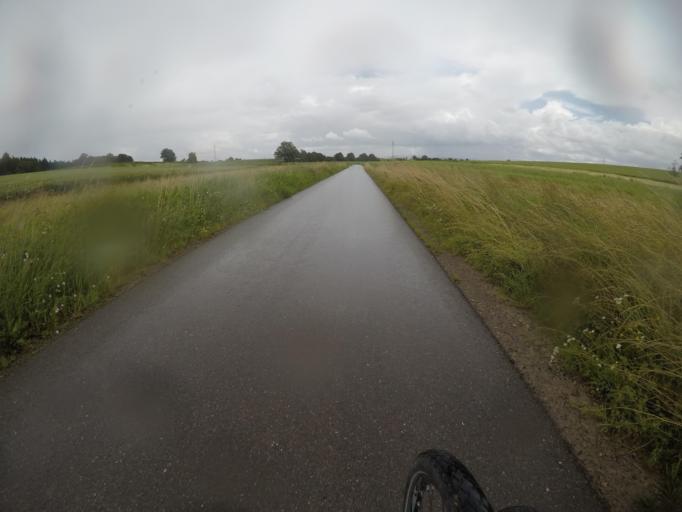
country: DE
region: Baden-Wuerttemberg
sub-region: Regierungsbezirk Stuttgart
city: Motzingen
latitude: 48.5109
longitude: 8.7955
